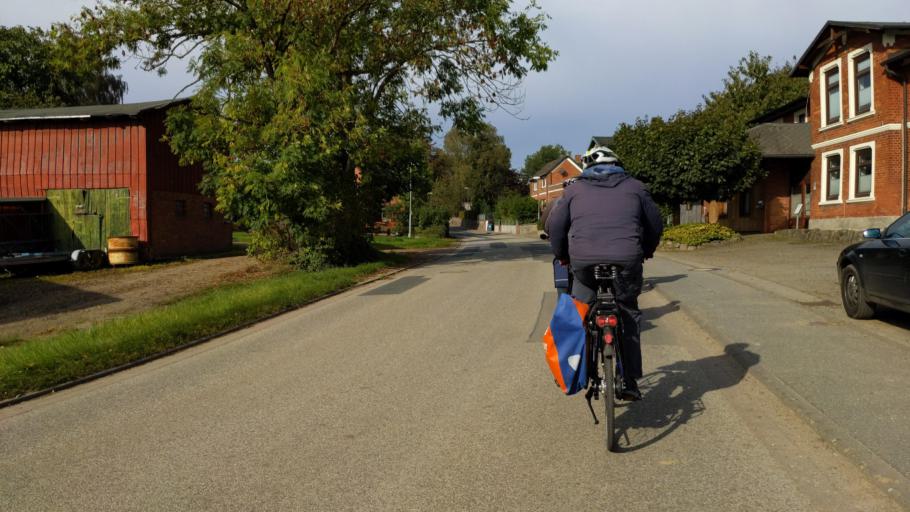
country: DE
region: Schleswig-Holstein
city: Zarpen
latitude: 53.8698
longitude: 10.5203
